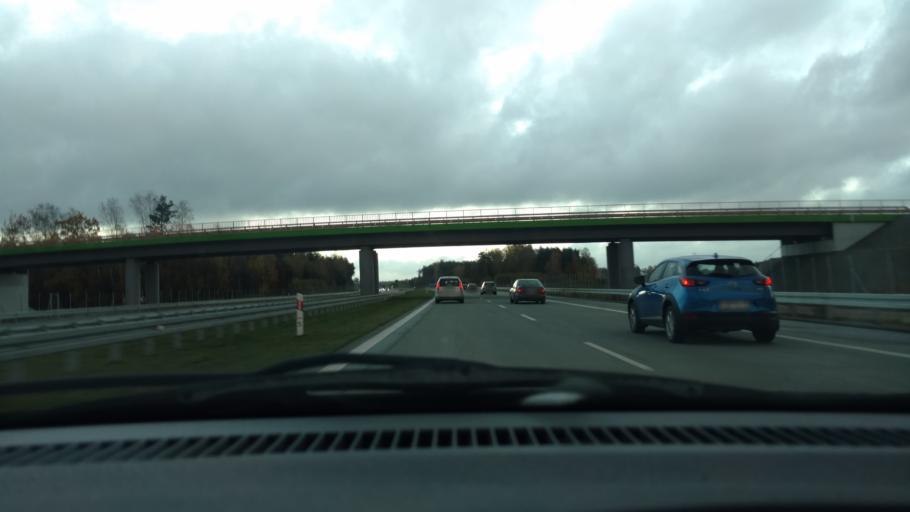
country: PL
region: Lodz Voivodeship
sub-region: Powiat lodzki wschodni
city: Andrespol
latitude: 51.7110
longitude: 19.6076
